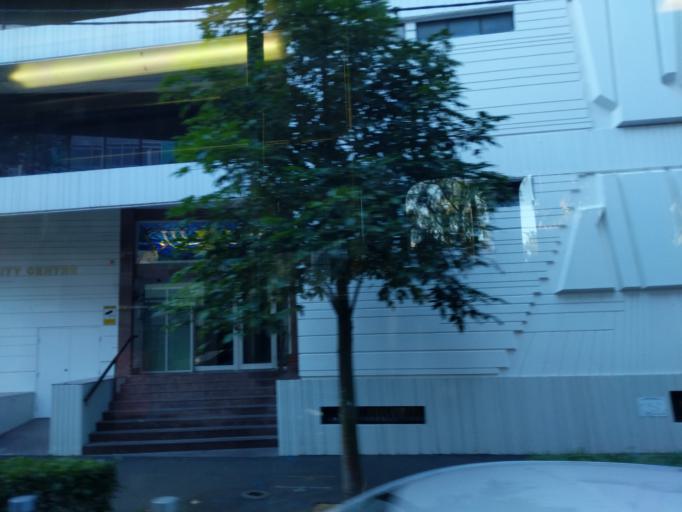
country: AU
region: New South Wales
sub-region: City of Sydney
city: Darlinghurst
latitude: -33.8788
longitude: 151.2201
